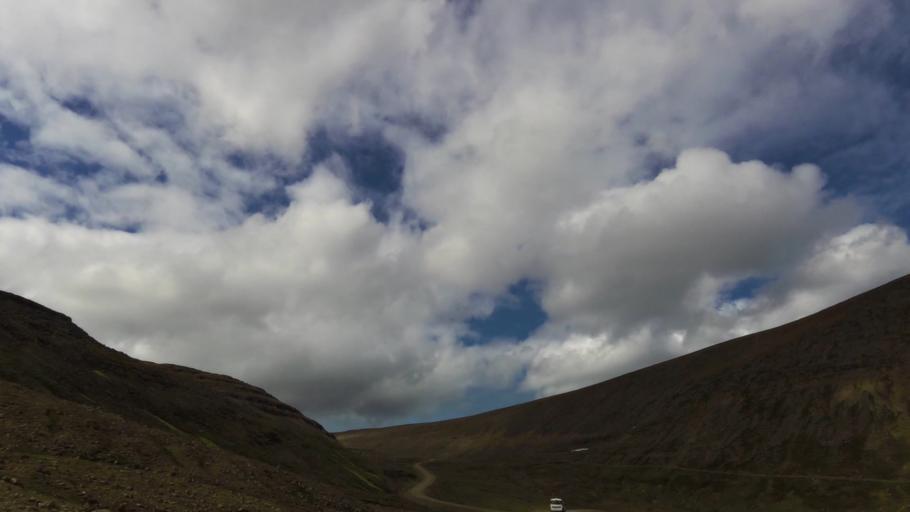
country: IS
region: Westfjords
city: Isafjoerdur
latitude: 66.1663
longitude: -23.3410
